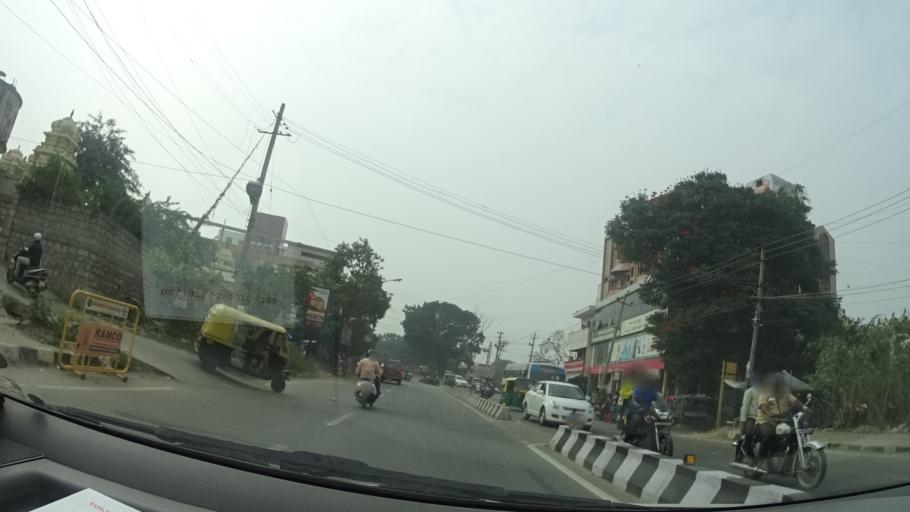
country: IN
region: Karnataka
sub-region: Bangalore Urban
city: Bangalore
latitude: 13.0217
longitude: 77.6289
